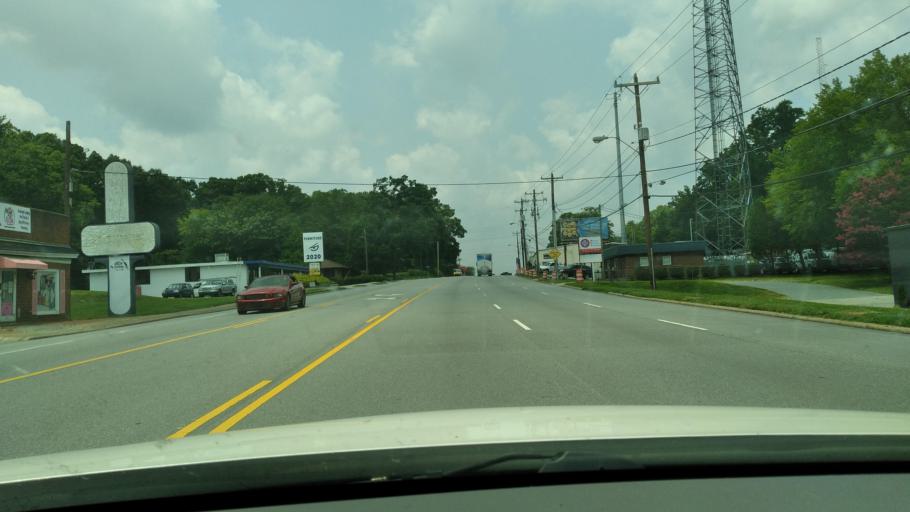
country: US
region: North Carolina
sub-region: Guilford County
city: Greensboro
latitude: 36.1172
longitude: -79.8385
